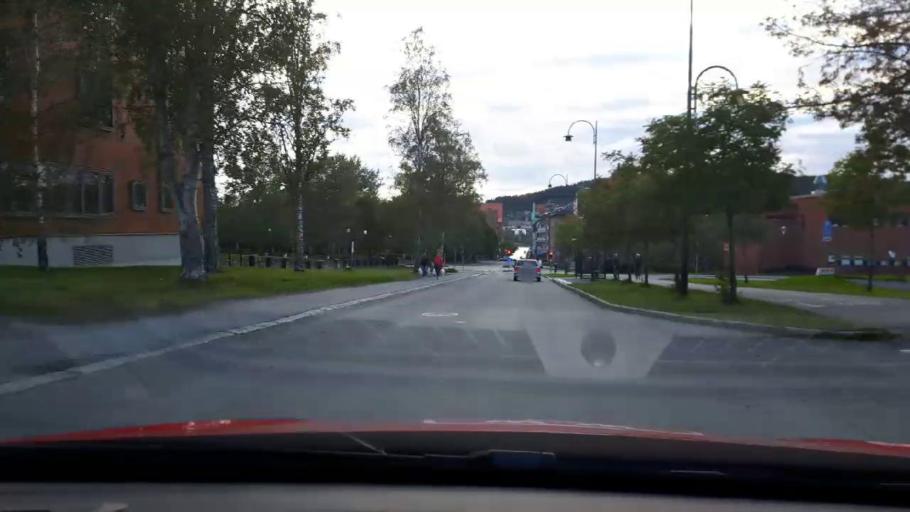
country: SE
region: Jaemtland
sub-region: OEstersunds Kommun
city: Ostersund
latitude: 63.1794
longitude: 14.6428
